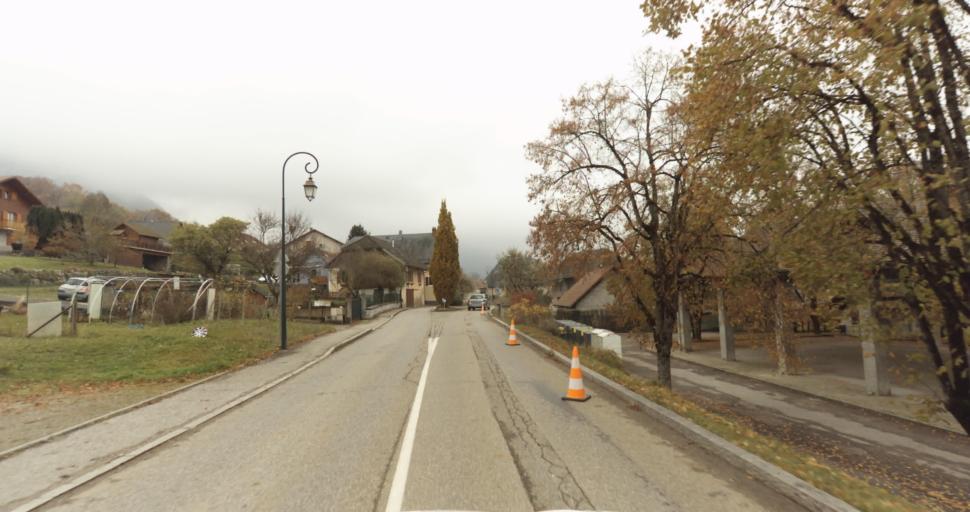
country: FR
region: Rhone-Alpes
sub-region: Departement de la Haute-Savoie
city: Gruffy
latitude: 45.7846
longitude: 6.0537
